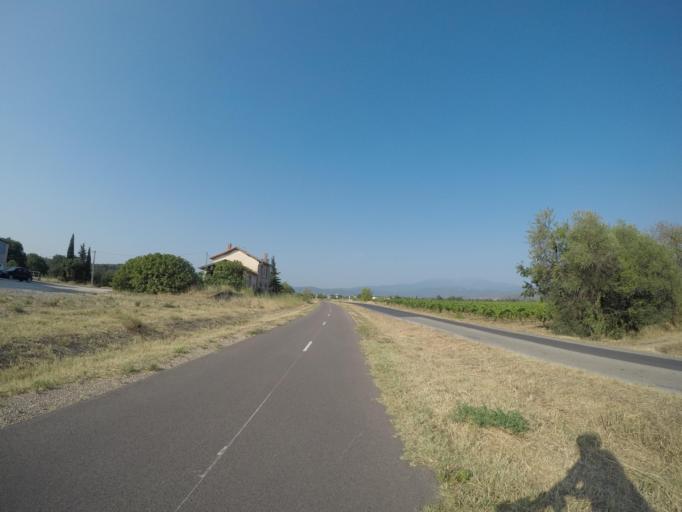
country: FR
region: Languedoc-Roussillon
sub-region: Departement des Pyrenees-Orientales
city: Ponteilla
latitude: 42.6289
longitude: 2.8041
